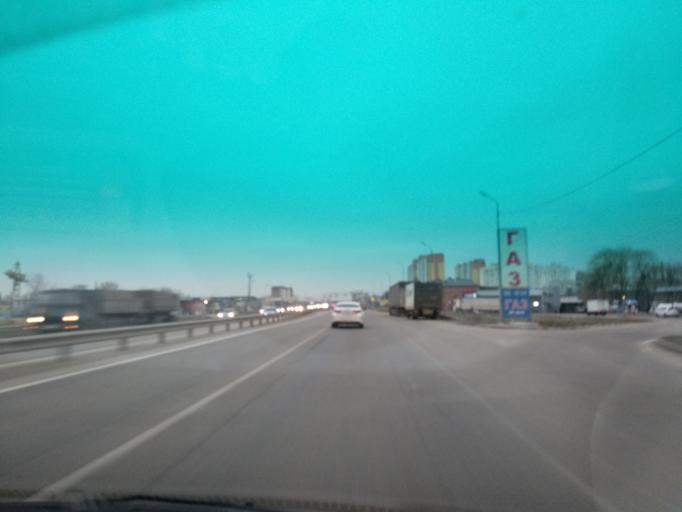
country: RU
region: Krasnodarskiy
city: Pashkovskiy
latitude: 45.0376
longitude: 39.1283
